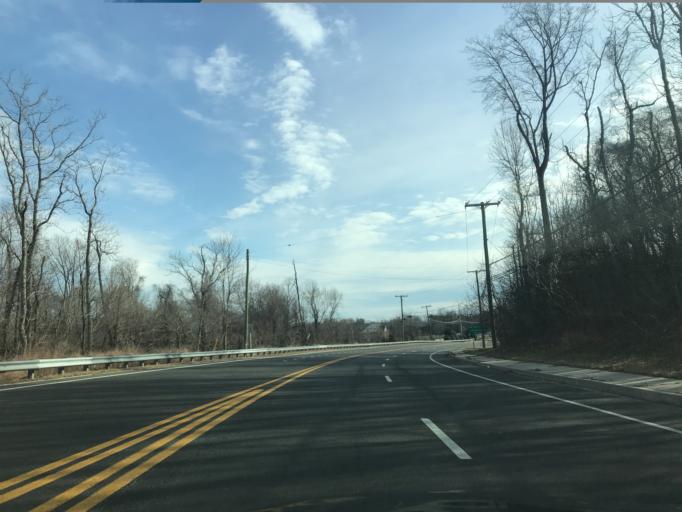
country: US
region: Maryland
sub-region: Prince George's County
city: Woodmore
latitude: 38.9238
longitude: -76.8038
